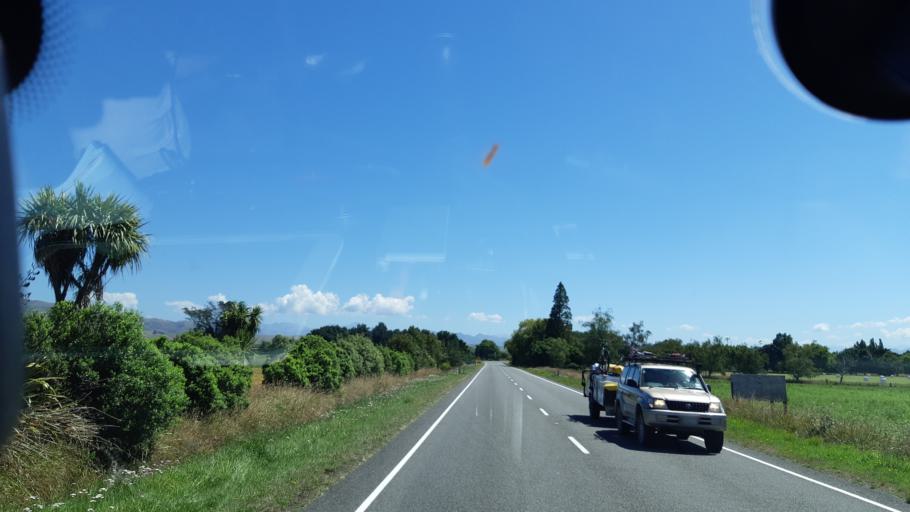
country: NZ
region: Canterbury
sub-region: Kaikoura District
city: Kaikoura
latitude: -42.7440
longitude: 173.2670
